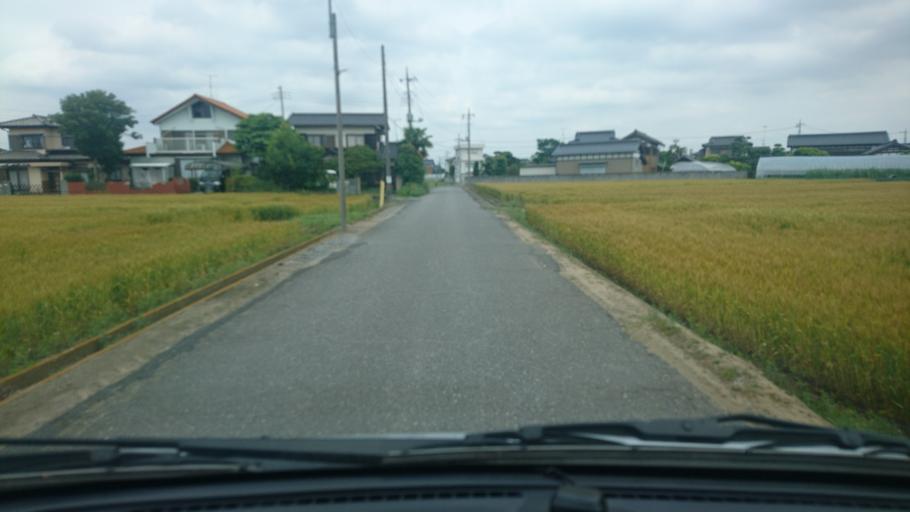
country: JP
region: Ibaraki
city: Ishige
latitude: 36.1010
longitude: 139.9777
